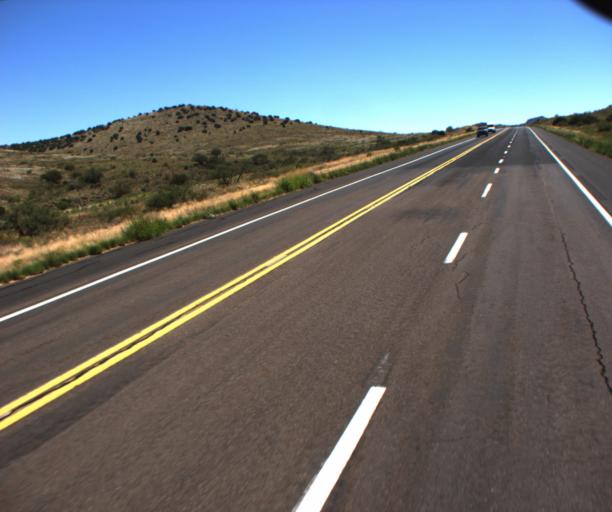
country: US
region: Arizona
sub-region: Greenlee County
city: Clifton
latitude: 32.8653
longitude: -109.2926
